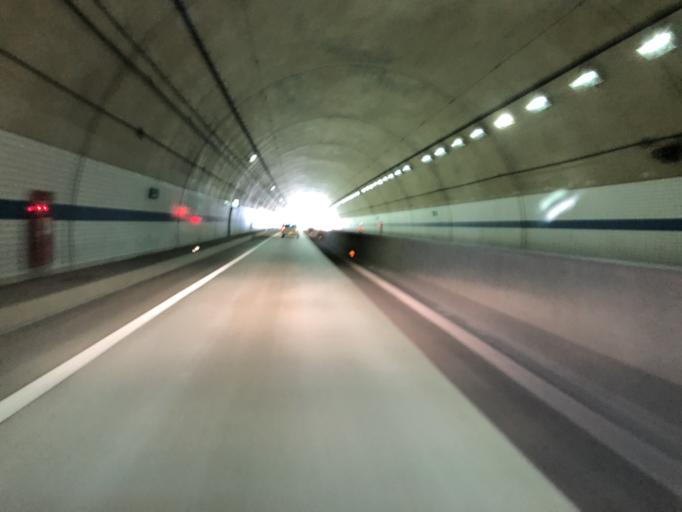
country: JP
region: Miyagi
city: Marumori
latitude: 37.7902
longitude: 140.7643
